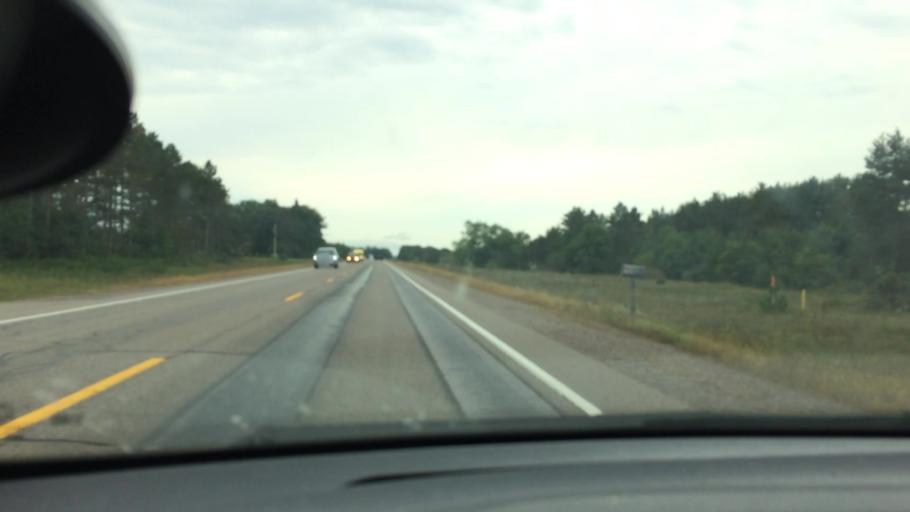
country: US
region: Wisconsin
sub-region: Eau Claire County
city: Augusta
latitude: 44.5842
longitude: -91.1042
